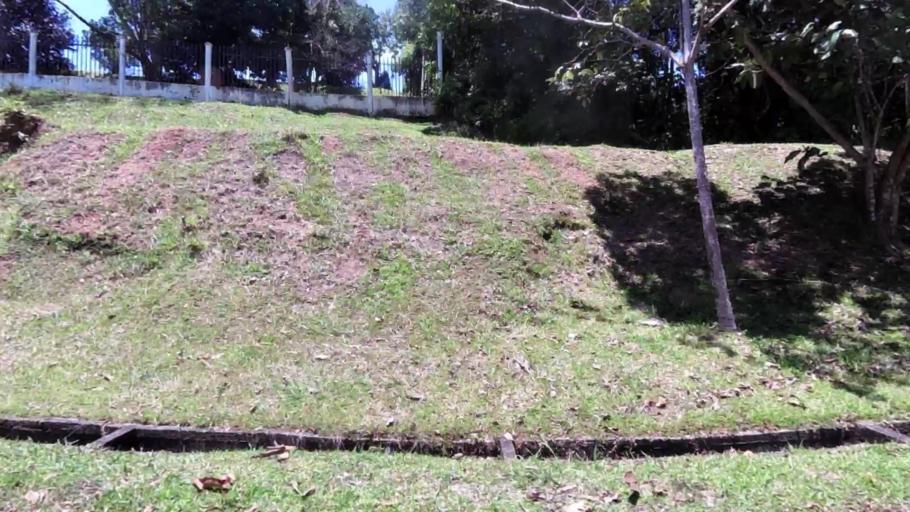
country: BN
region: Brunei and Muara
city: Bandar Seri Begawan
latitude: 4.9303
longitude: 114.9620
